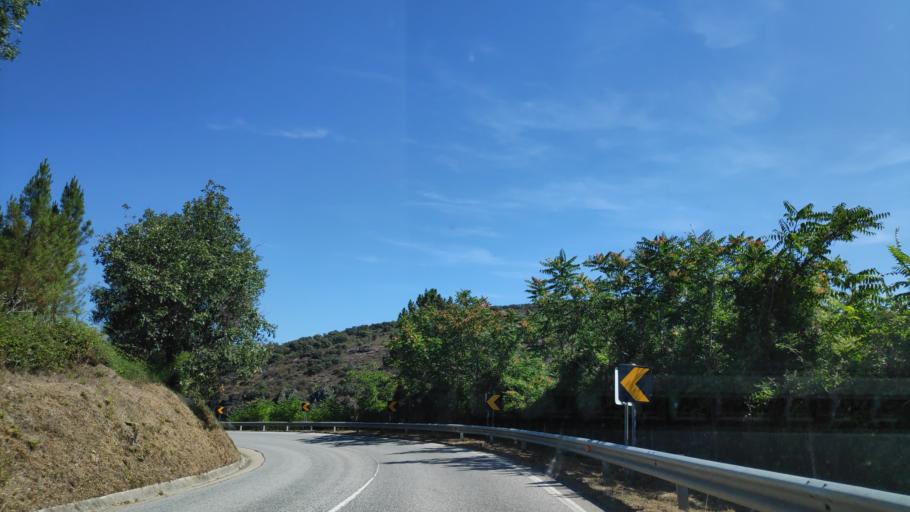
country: PT
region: Braganca
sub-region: Braganca Municipality
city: Braganca
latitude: 41.8295
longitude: -6.7467
